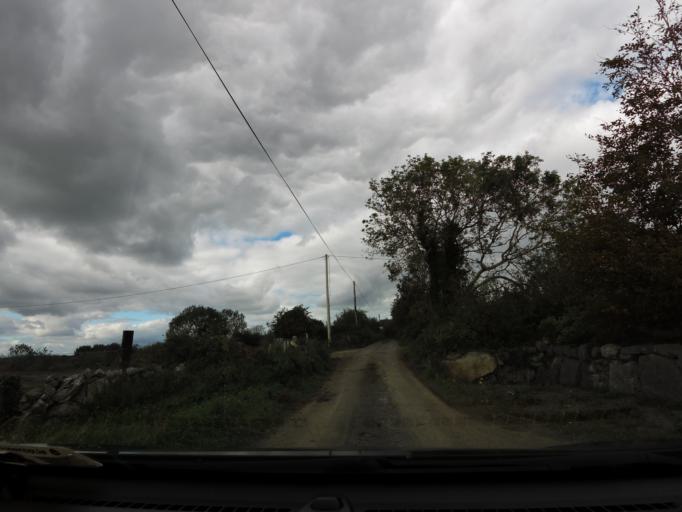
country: IE
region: Connaught
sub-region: County Galway
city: Moycullen
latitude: 53.3357
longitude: -9.1394
